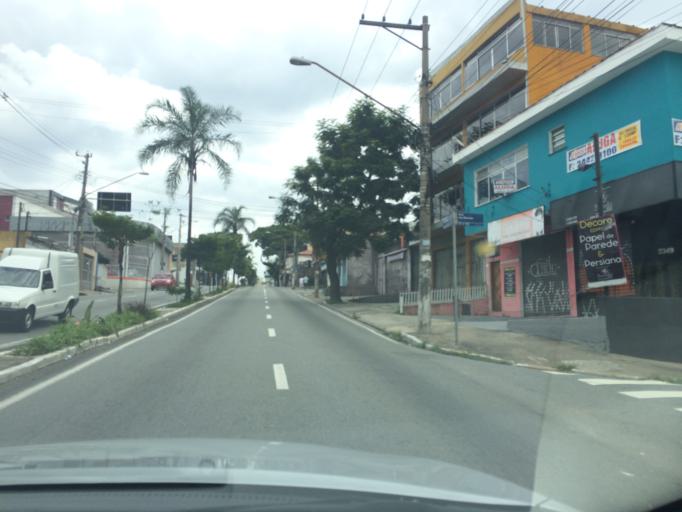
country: BR
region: Sao Paulo
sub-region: Guarulhos
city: Guarulhos
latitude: -23.4597
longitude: -46.5222
